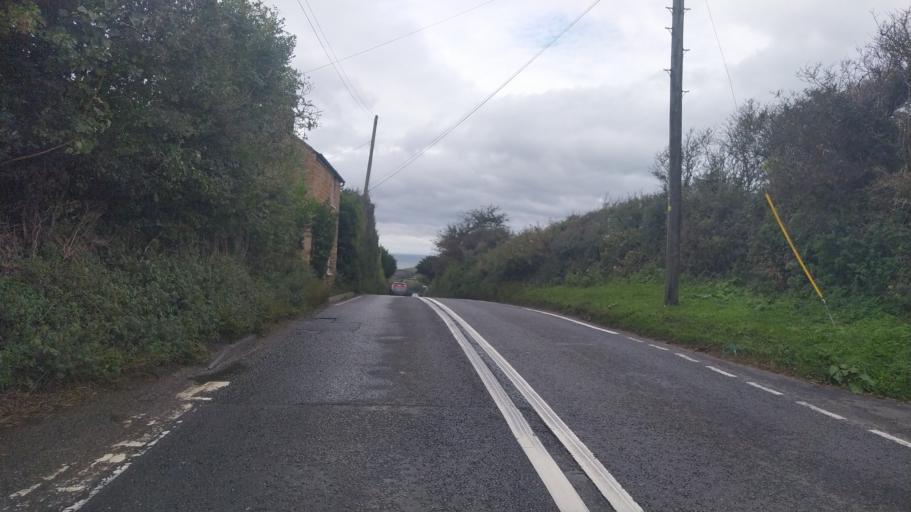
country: GB
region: England
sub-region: Dorset
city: Bridport
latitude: 50.7320
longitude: -2.7995
